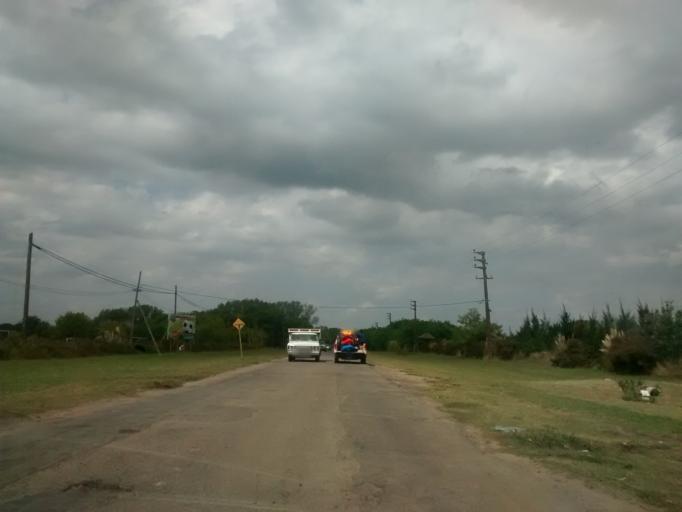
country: AR
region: Buenos Aires
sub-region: Partido de La Plata
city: La Plata
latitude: -34.9917
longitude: -57.9157
